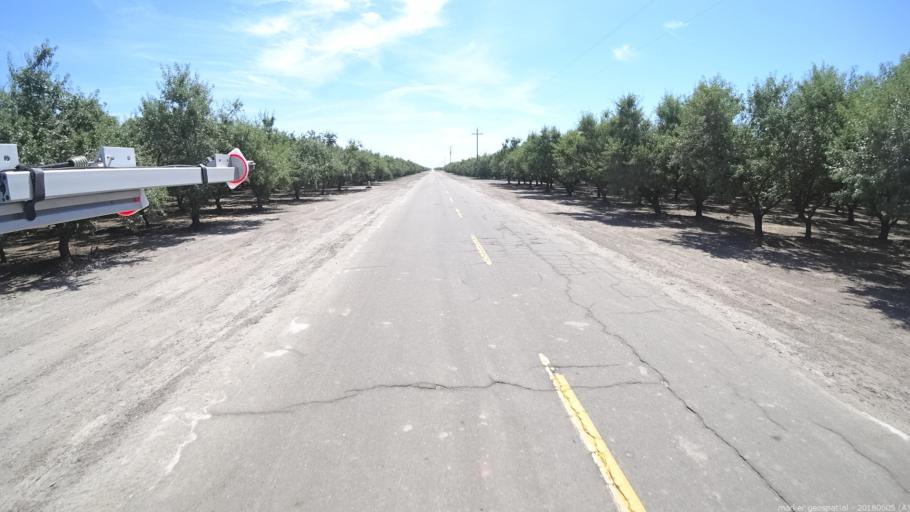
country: US
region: California
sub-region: Madera County
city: Chowchilla
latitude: 37.0983
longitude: -120.4312
